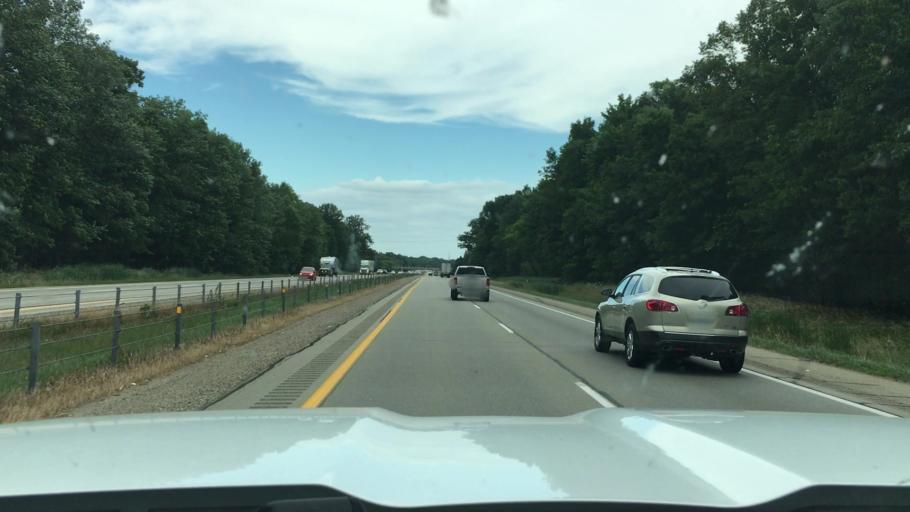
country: US
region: Michigan
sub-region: Allegan County
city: Wayland
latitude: 42.7469
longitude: -85.6734
